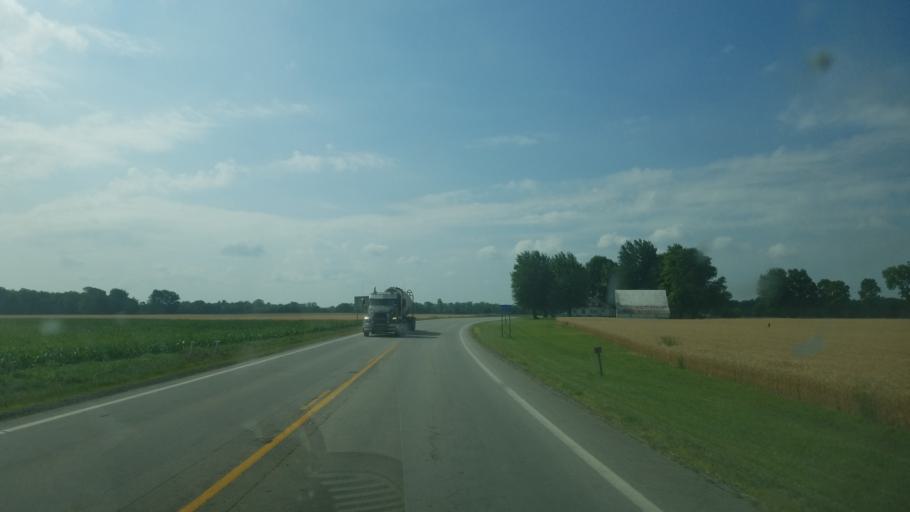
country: US
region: Ohio
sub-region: Logan County
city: Russells Point
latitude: 40.5288
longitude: -83.8304
